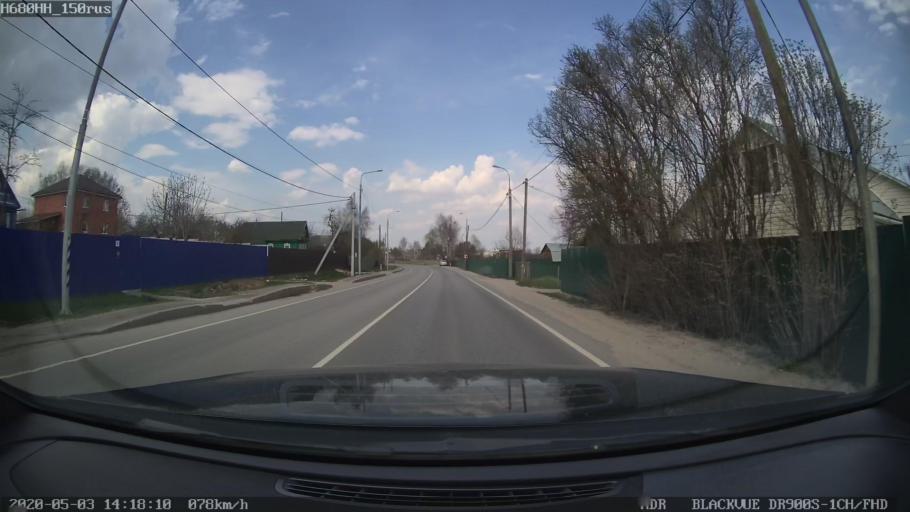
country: RU
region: Moskovskaya
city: Solnechnogorsk
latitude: 56.2156
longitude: 36.9731
